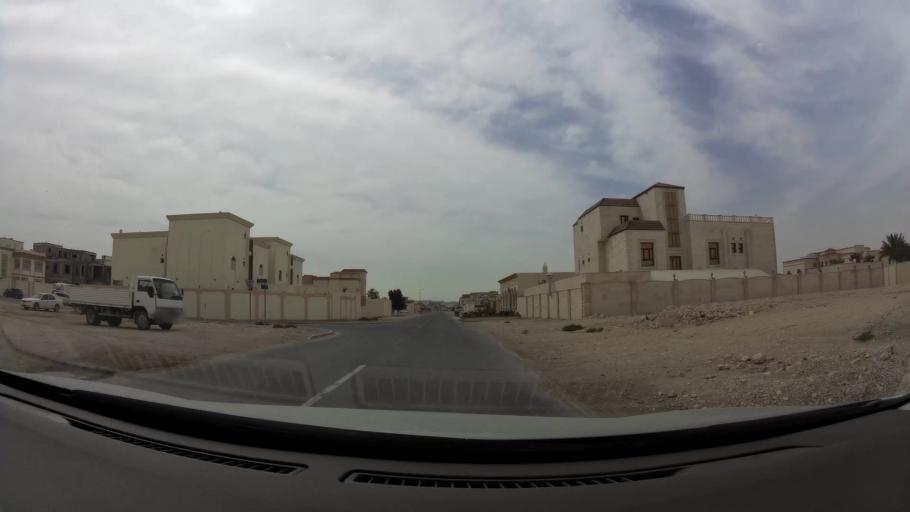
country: QA
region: Baladiyat ad Dawhah
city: Doha
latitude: 25.2143
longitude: 51.4724
